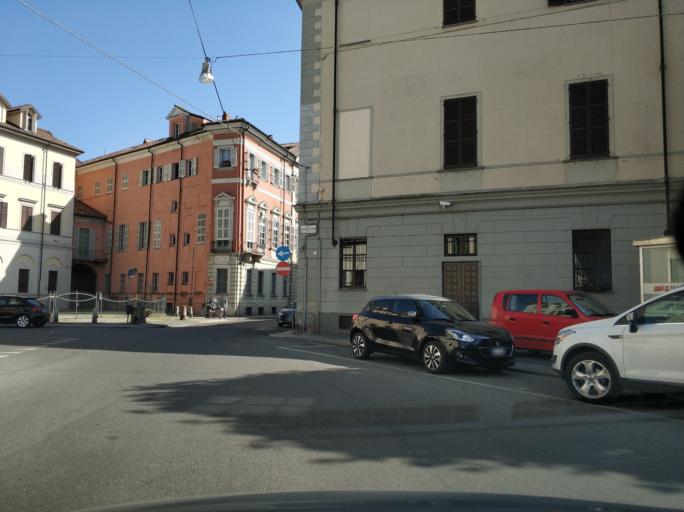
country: IT
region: Piedmont
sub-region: Provincia di Vercelli
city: Vercelli
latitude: 45.3292
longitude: 8.4233
